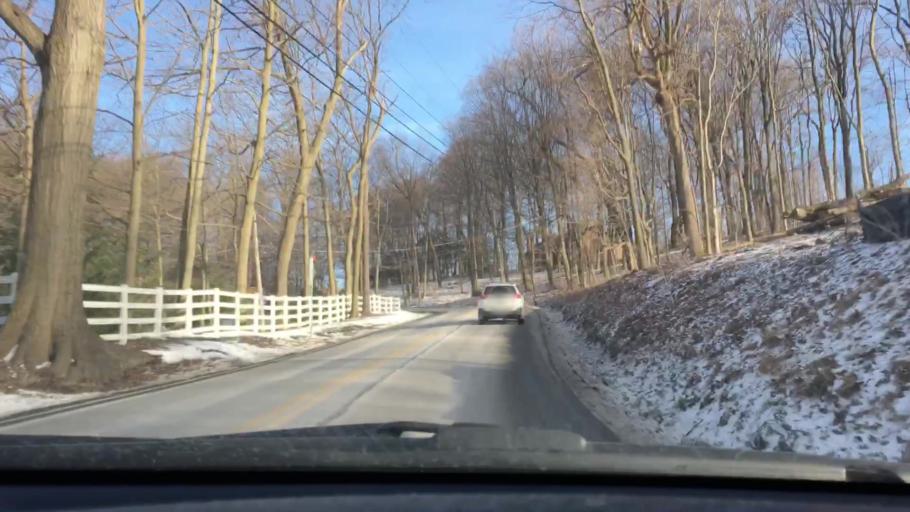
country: US
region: Pennsylvania
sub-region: Washington County
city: McMurray
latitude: 40.2827
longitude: -80.0512
